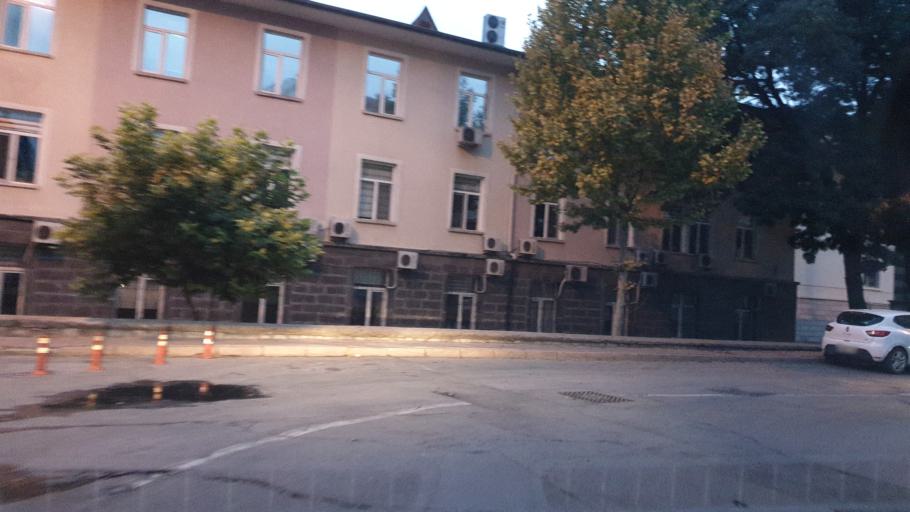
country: TR
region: Kayseri
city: Kayseri
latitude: 38.7263
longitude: 35.4791
